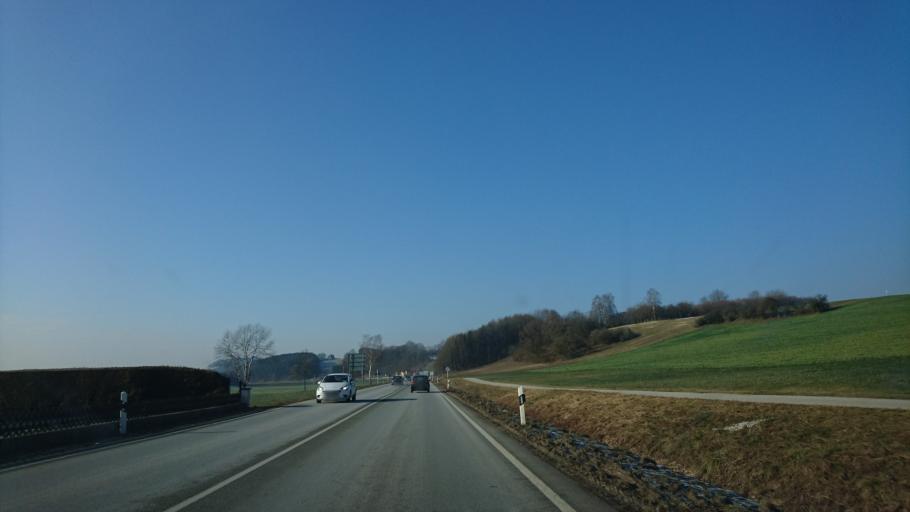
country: DE
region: Bavaria
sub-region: Lower Bavaria
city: Bad Birnbach
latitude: 48.4476
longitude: 13.0390
